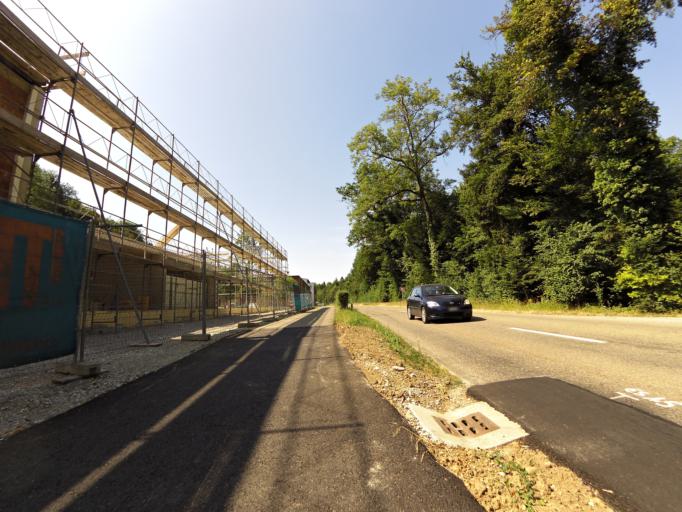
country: CH
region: Aargau
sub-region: Bezirk Brugg
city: Windisch
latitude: 47.4683
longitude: 8.2302
